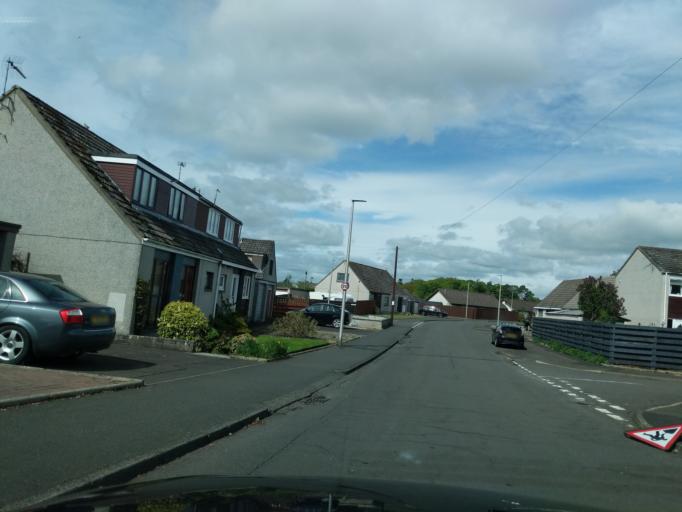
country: GB
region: Scotland
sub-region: The Scottish Borders
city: Kelso
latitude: 55.6065
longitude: -2.4370
